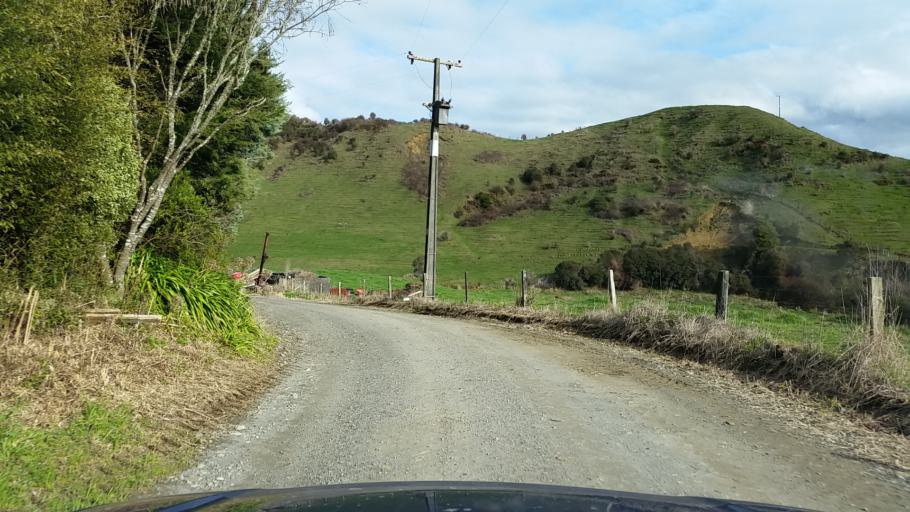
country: NZ
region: Taranaki
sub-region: South Taranaki District
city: Eltham
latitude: -39.2569
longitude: 174.5740
